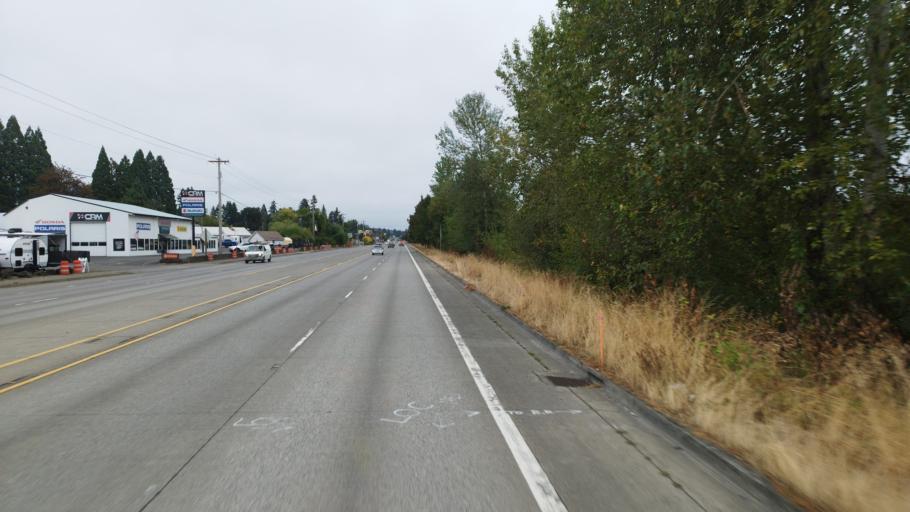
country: US
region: Oregon
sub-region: Columbia County
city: Warren
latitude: 45.8395
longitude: -122.8371
